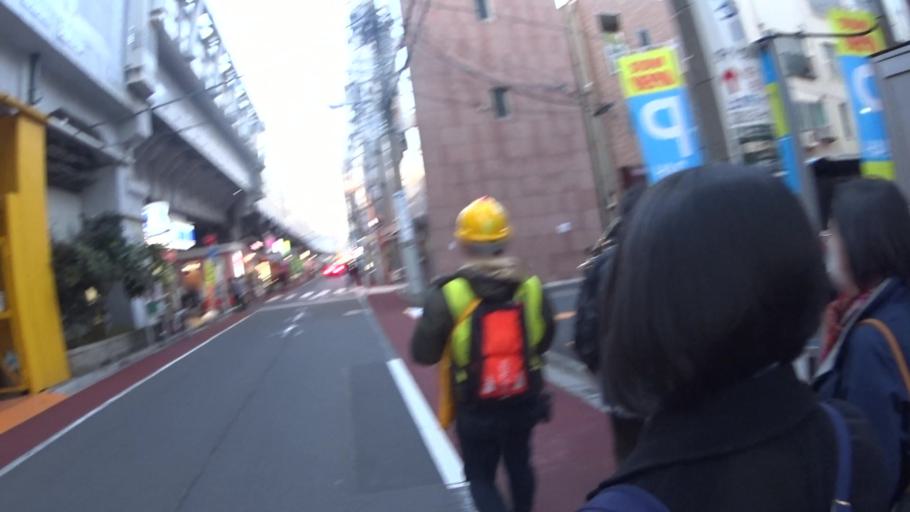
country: JP
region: Tokyo
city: Tokyo
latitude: 35.7044
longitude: 139.7753
